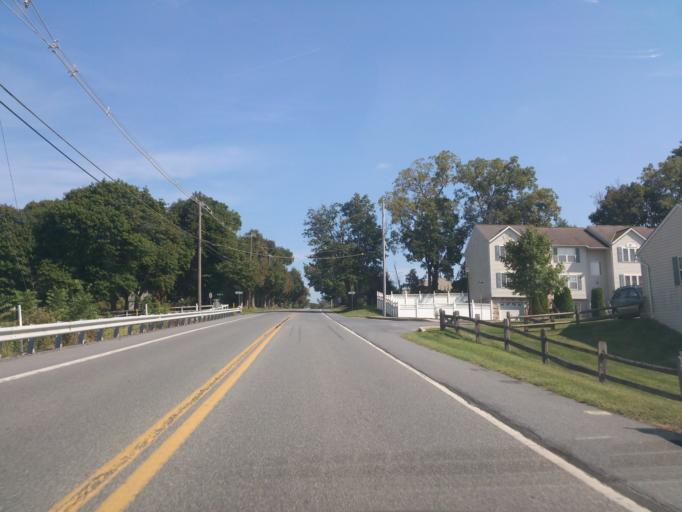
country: US
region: Pennsylvania
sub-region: Lebanon County
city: Cornwall
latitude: 40.2771
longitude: -76.4306
